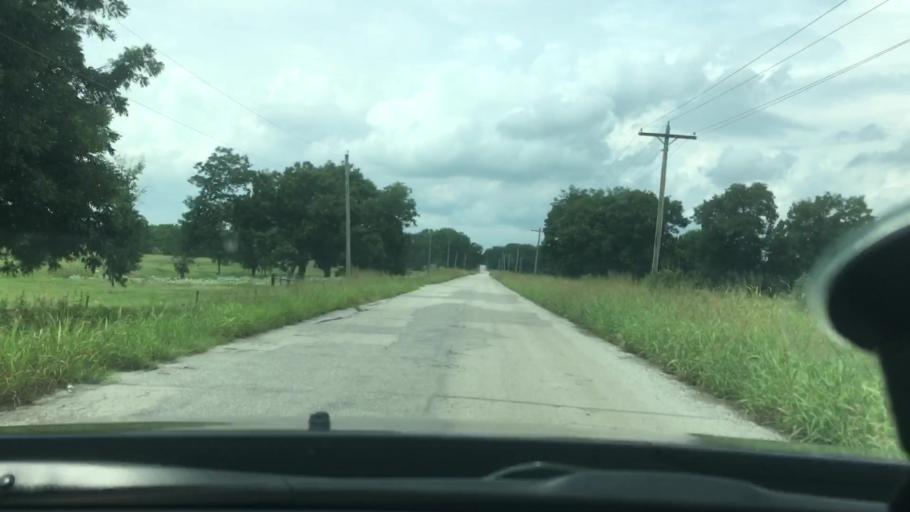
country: US
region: Oklahoma
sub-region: Carter County
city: Dickson
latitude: 34.2527
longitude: -96.9448
